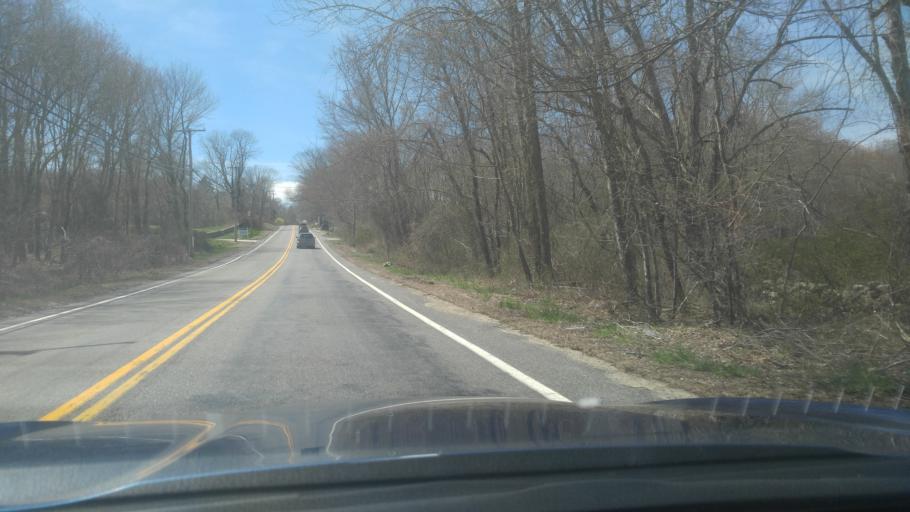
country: US
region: Rhode Island
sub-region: Washington County
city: Exeter
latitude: 41.5796
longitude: -71.5828
